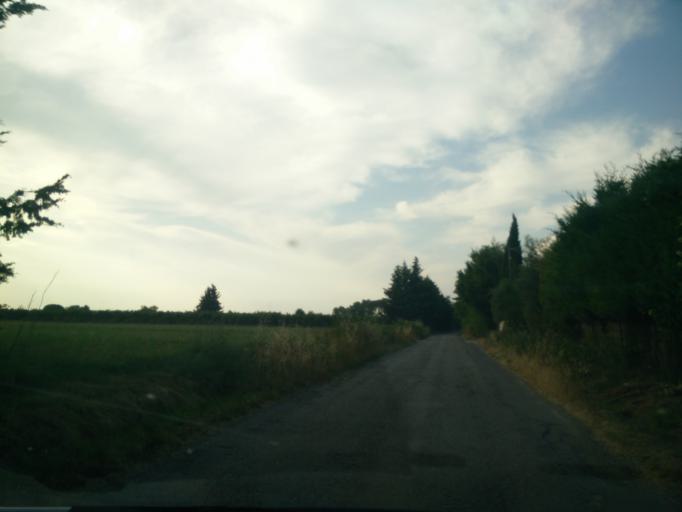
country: FR
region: Languedoc-Roussillon
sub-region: Departement de l'Herault
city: Marsillargues
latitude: 43.6770
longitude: 4.1731
